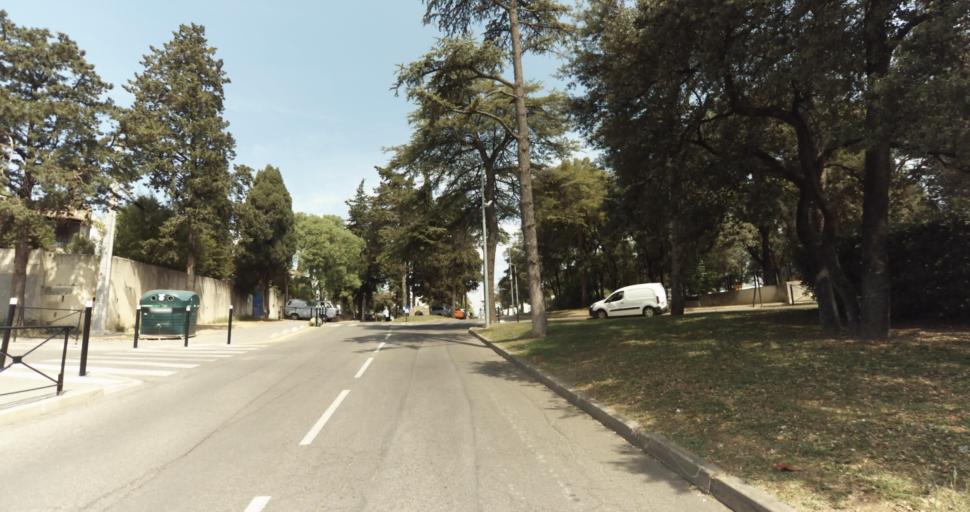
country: FR
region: Languedoc-Roussillon
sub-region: Departement du Gard
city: Nimes
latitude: 43.8446
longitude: 4.3649
